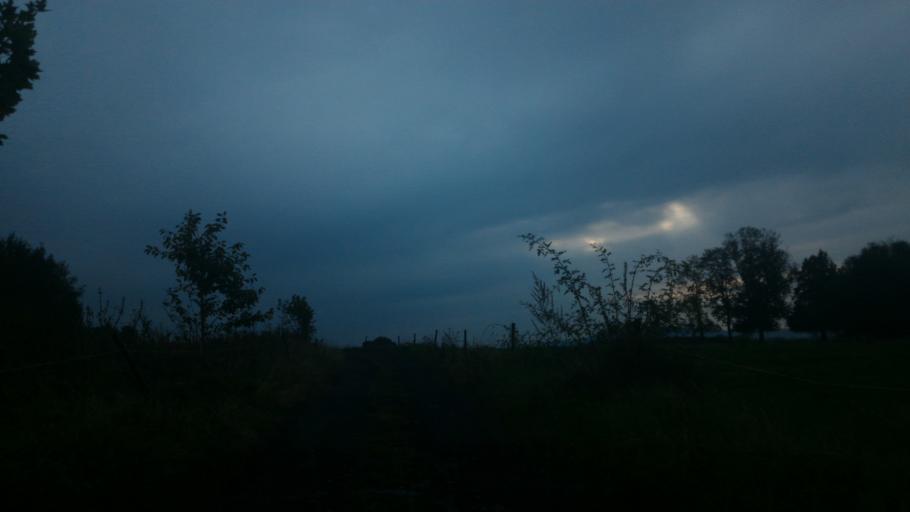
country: CZ
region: Ustecky
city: Dolni Podluzi
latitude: 50.8990
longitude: 14.5651
